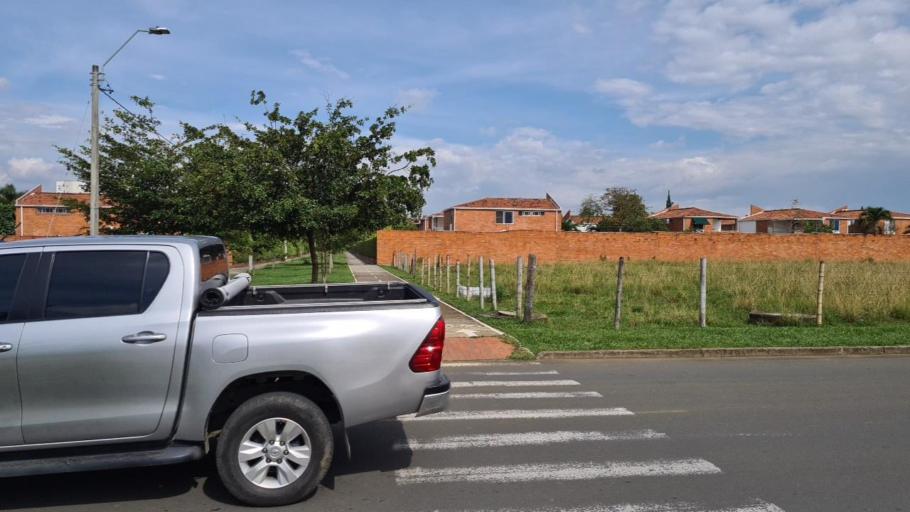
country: CO
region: Valle del Cauca
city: Jamundi
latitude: 3.2571
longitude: -76.5631
